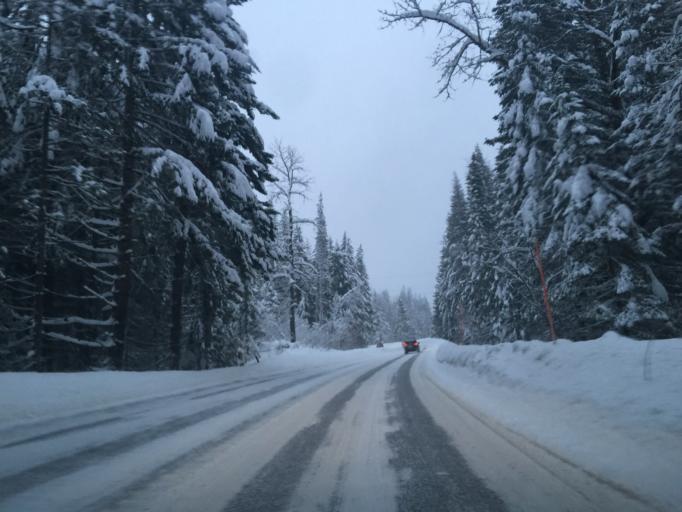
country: US
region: Washington
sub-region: Chelan County
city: Leavenworth
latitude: 47.7819
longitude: -120.9386
